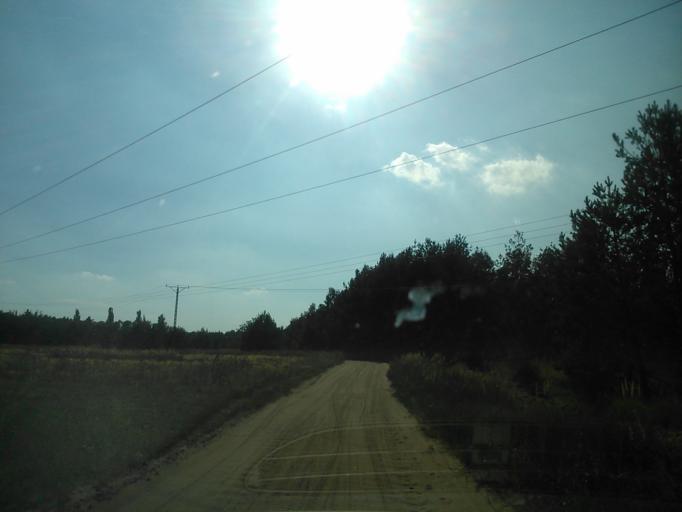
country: PL
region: Kujawsko-Pomorskie
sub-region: Powiat golubsko-dobrzynski
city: Golub-Dobrzyn
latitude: 53.1140
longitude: 19.0762
